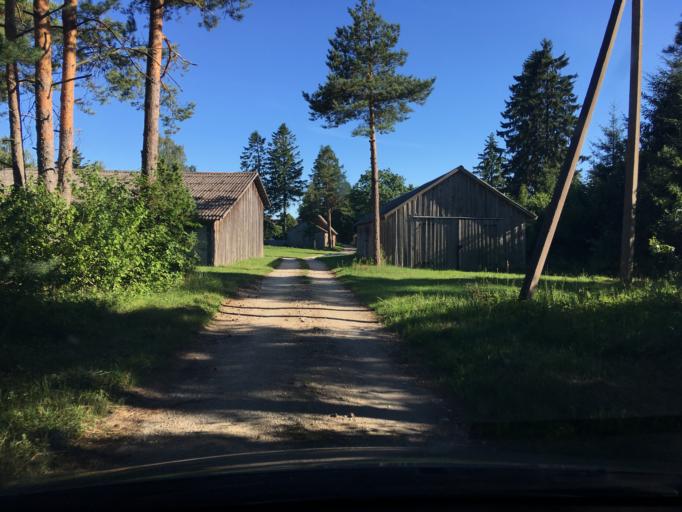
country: EE
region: Laeaene
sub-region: Lihula vald
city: Lihula
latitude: 58.5839
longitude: 23.7362
